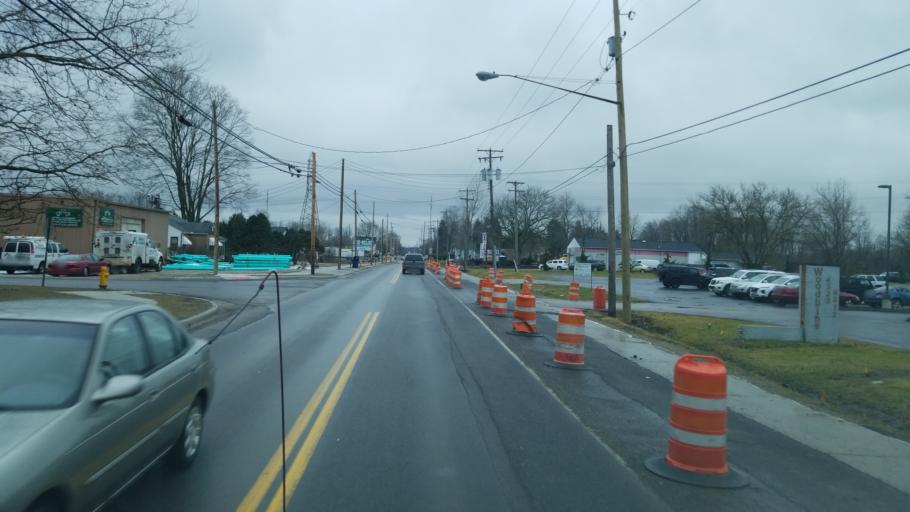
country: US
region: Ohio
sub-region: Summit County
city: Norton
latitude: 41.0211
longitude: -81.6384
